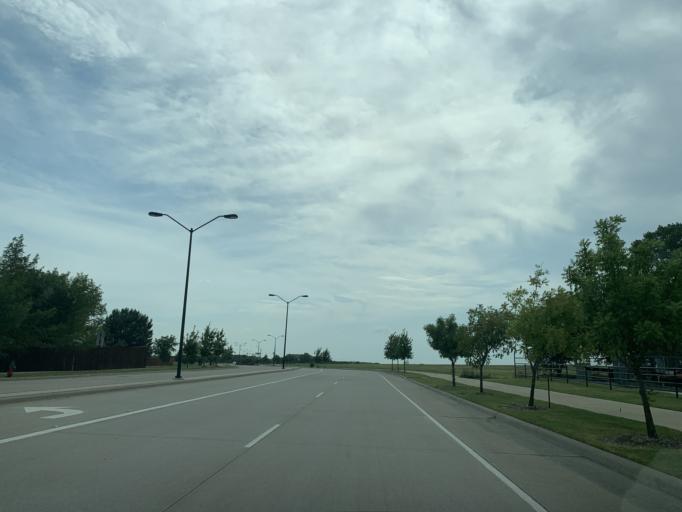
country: US
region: Texas
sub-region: Tarrant County
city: Watauga
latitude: 32.8367
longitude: -97.2792
